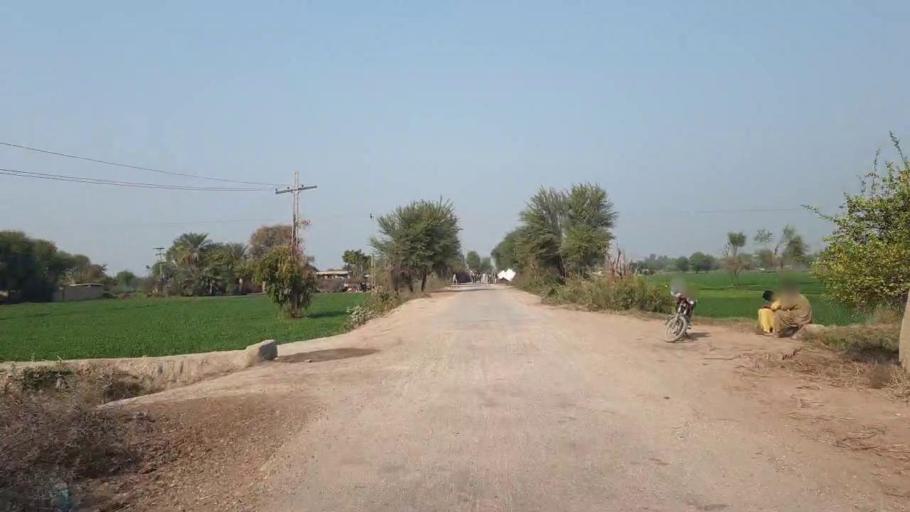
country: PK
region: Sindh
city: Hala
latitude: 25.8456
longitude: 68.4616
